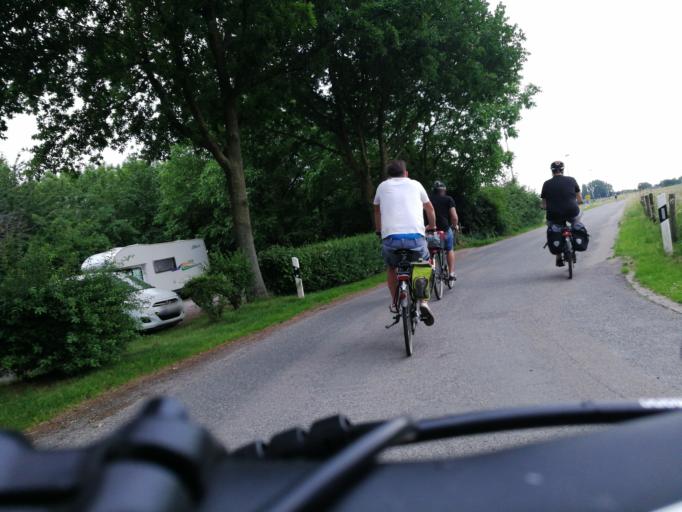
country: DE
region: North Rhine-Westphalia
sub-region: Regierungsbezirk Dusseldorf
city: Kleve
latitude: 51.8356
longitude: 6.1122
